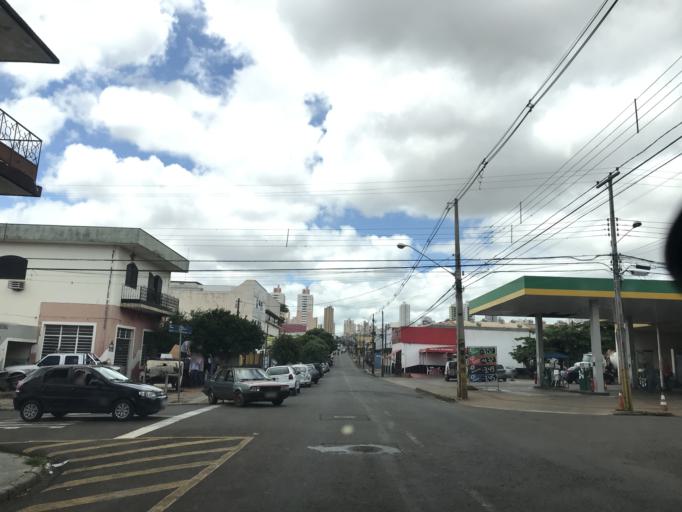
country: BR
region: Parana
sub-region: Londrina
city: Londrina
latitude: -23.2970
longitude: -51.1628
